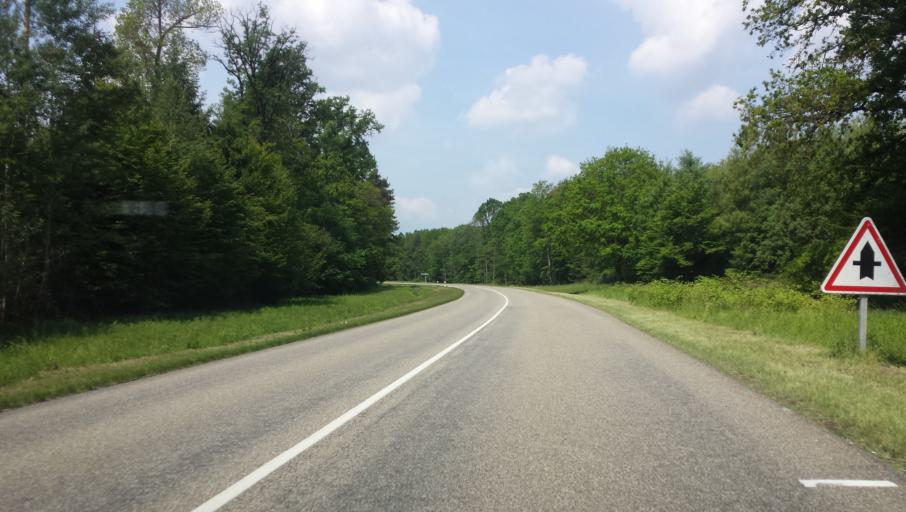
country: DE
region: Rheinland-Pfalz
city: Scheibenhardt
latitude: 48.9864
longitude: 8.1058
